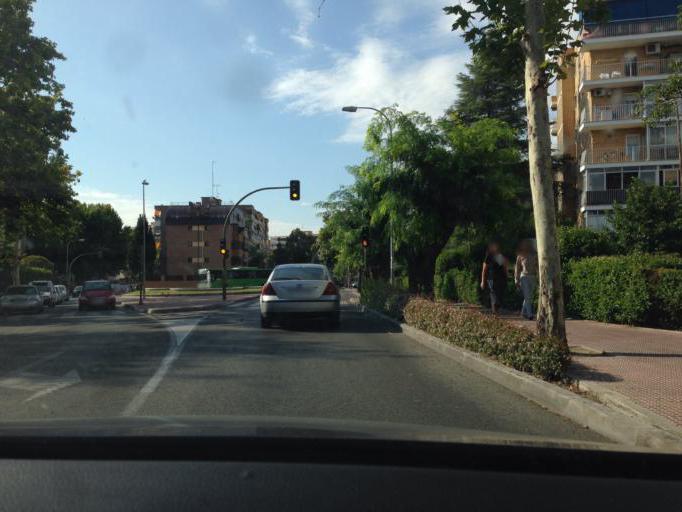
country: ES
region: Madrid
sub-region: Provincia de Madrid
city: Alcala de Henares
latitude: 40.4936
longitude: -3.3778
